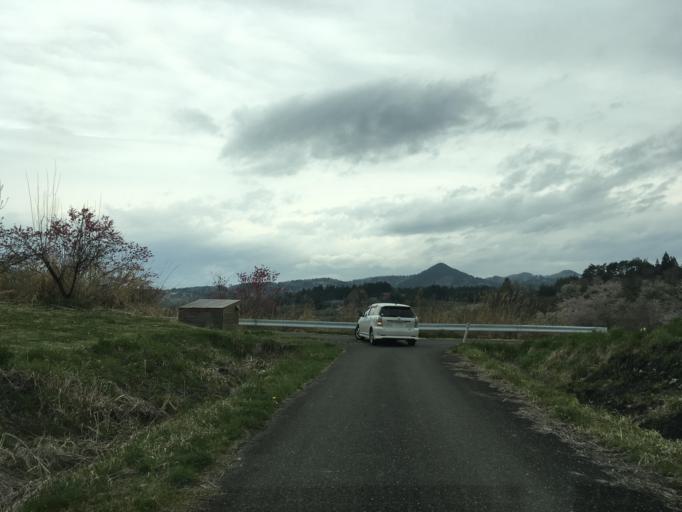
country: JP
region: Iwate
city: Ichinoseki
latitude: 38.8504
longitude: 141.3294
